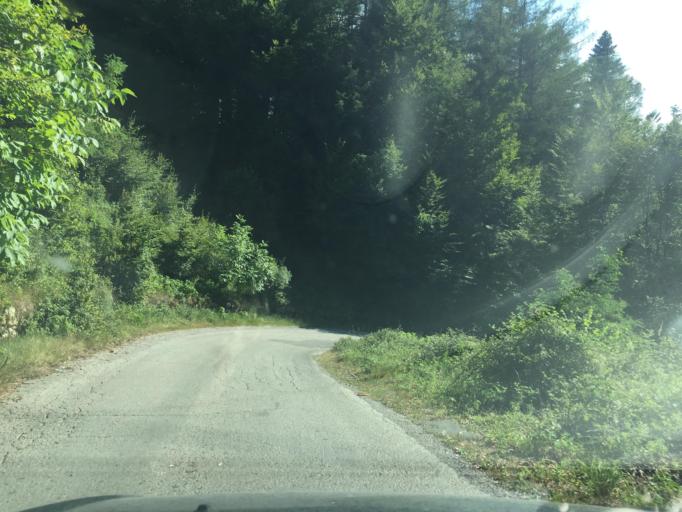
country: HR
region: Primorsko-Goranska
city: Klana
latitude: 45.4688
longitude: 14.3854
